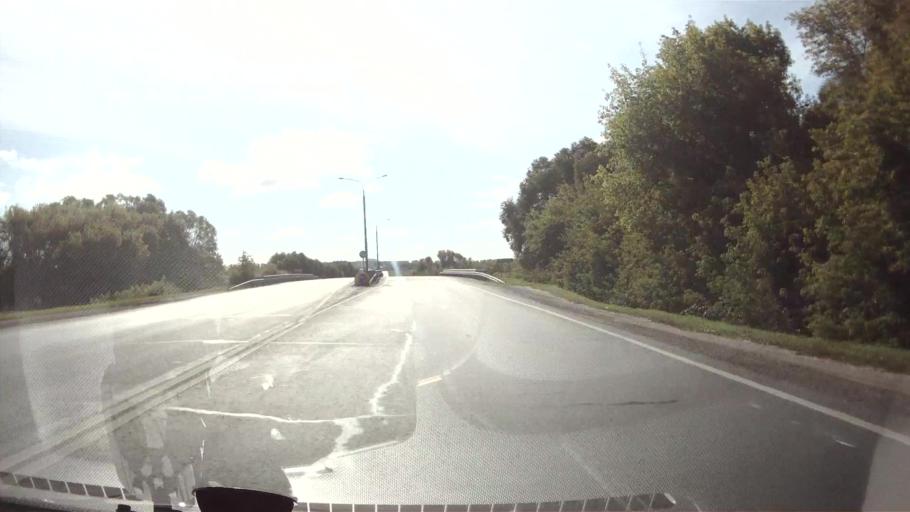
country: RU
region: Ulyanovsk
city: Isheyevka
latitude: 54.3050
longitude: 48.2407
